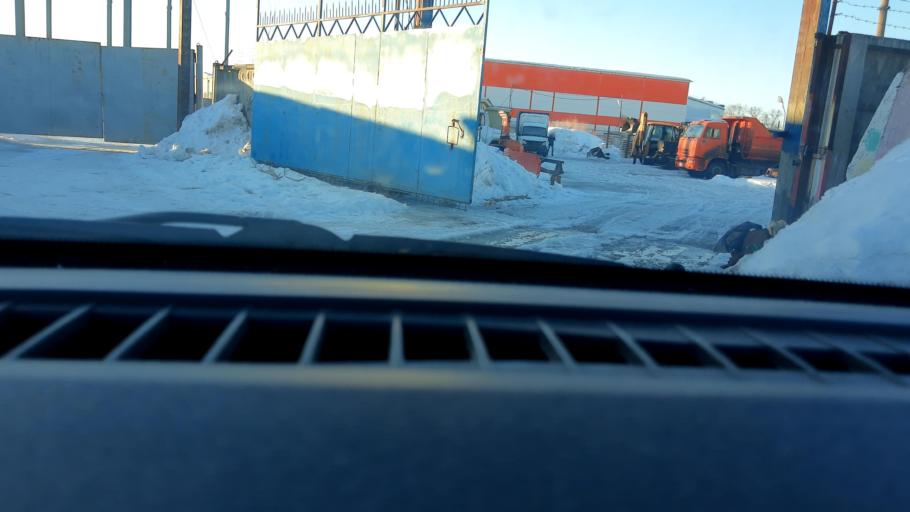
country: RU
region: Nizjnij Novgorod
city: Nizhniy Novgorod
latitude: 56.3031
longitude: 43.8882
